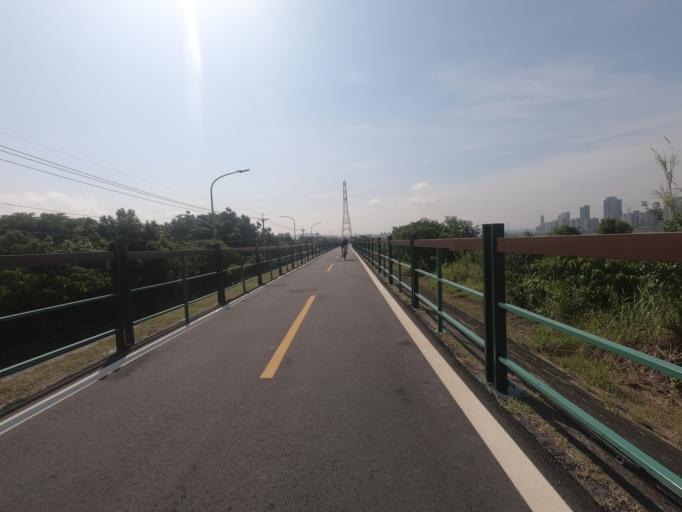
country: TW
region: Taipei
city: Taipei
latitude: 25.1013
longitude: 121.4866
